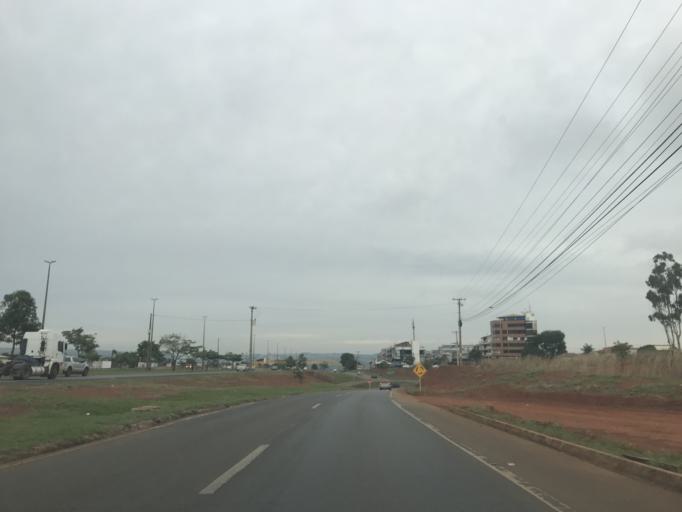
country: BR
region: Federal District
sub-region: Brasilia
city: Brasilia
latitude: -15.6825
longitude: -47.8390
